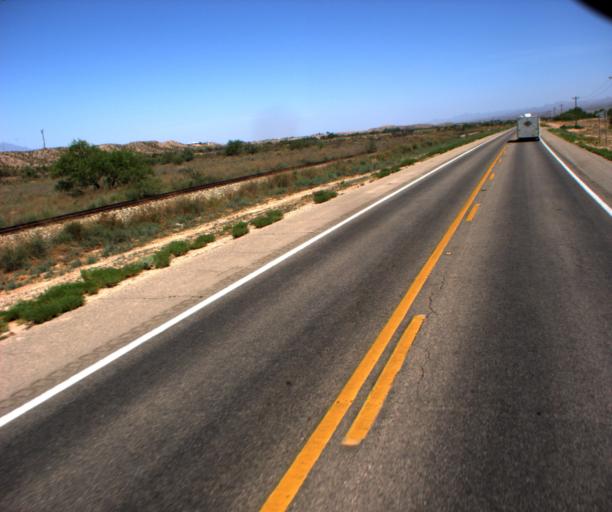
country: US
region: Arizona
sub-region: Graham County
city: Pima
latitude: 32.9930
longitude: -109.9387
